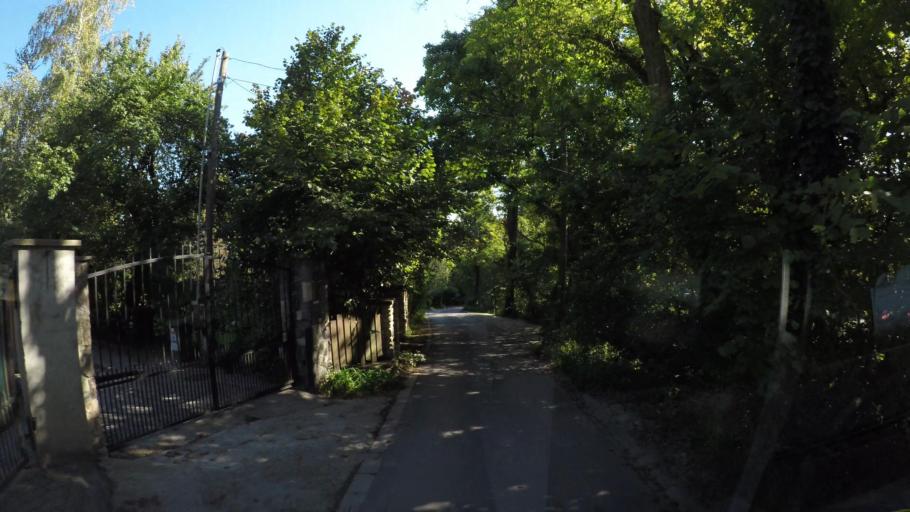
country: HU
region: Pest
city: Leanyfalu
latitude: 47.7268
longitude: 19.0854
